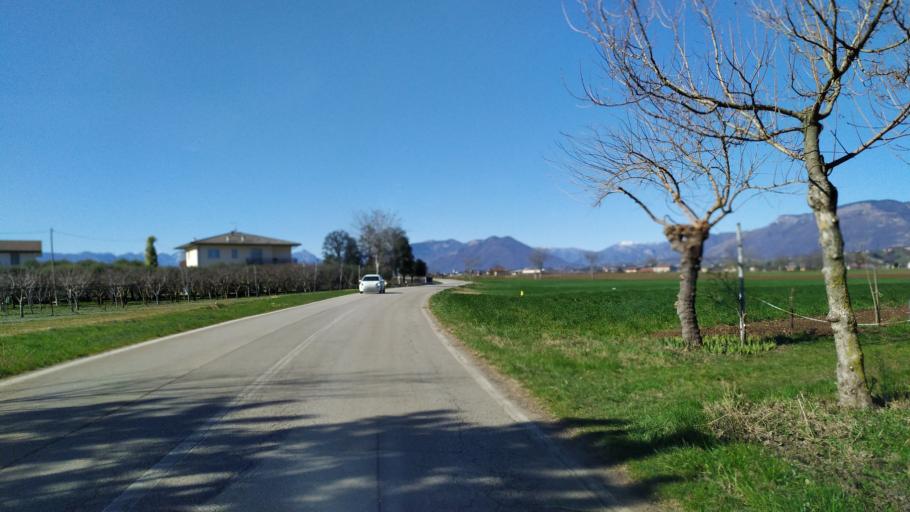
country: IT
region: Veneto
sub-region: Provincia di Vicenza
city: Sandrigo
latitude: 45.6886
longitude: 11.5872
